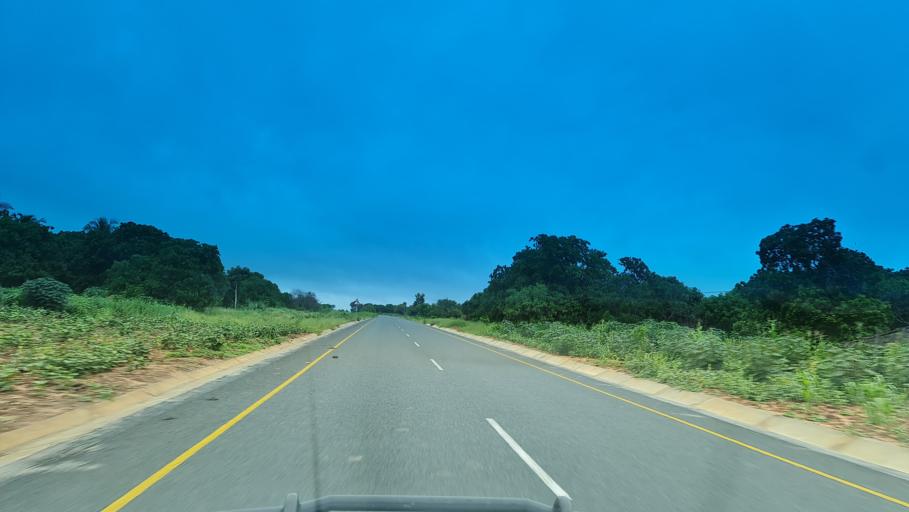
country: MZ
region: Nampula
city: Nampula
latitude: -15.6012
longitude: 39.3271
